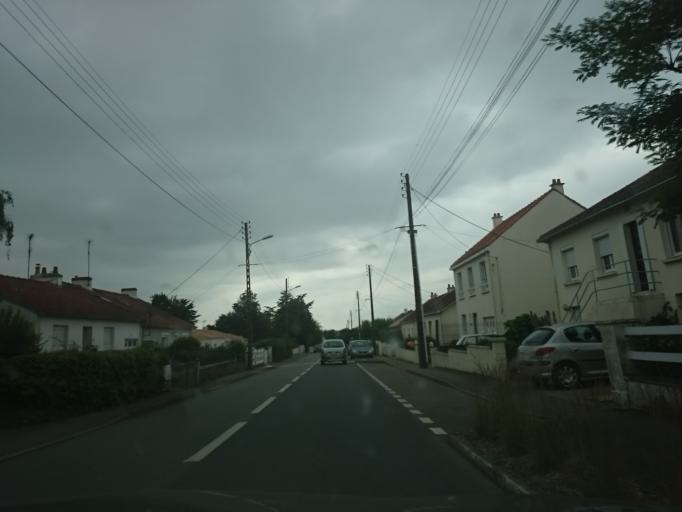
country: FR
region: Pays de la Loire
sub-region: Departement de la Loire-Atlantique
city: Saint-Jean-de-Boiseau
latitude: 47.1926
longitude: -1.7166
